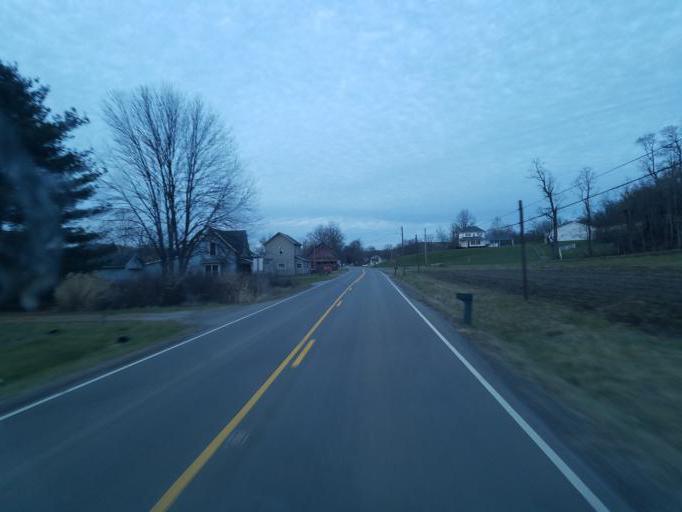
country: US
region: Ohio
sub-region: Muskingum County
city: Dresden
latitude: 40.1951
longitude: -82.0445
